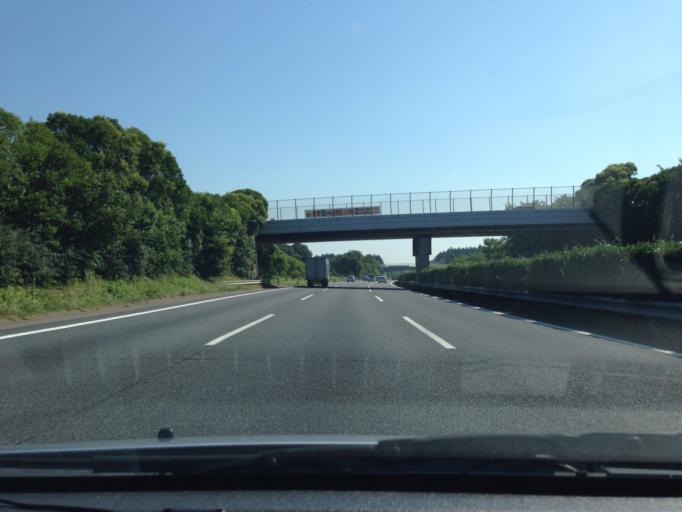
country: JP
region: Ibaraki
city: Ishioka
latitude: 36.2046
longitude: 140.2652
